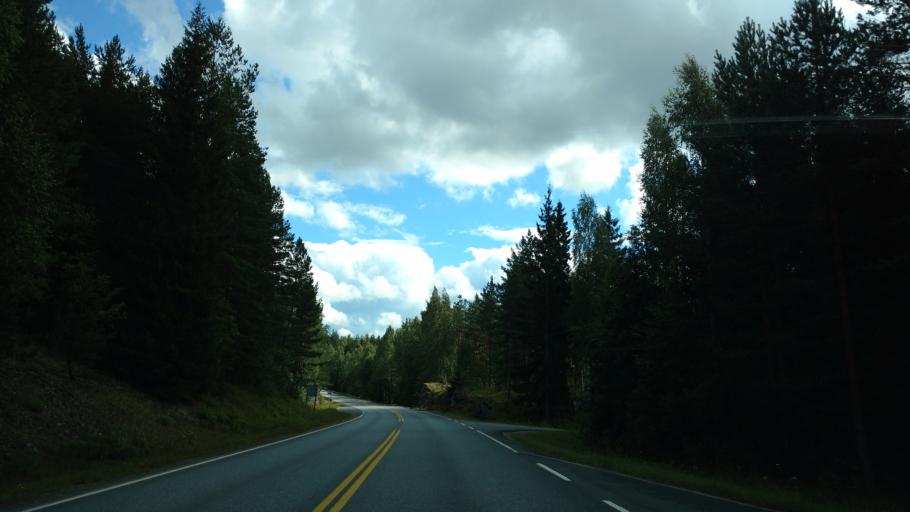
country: FI
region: Uusimaa
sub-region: Helsinki
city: Karjalohja
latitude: 60.2181
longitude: 23.6265
